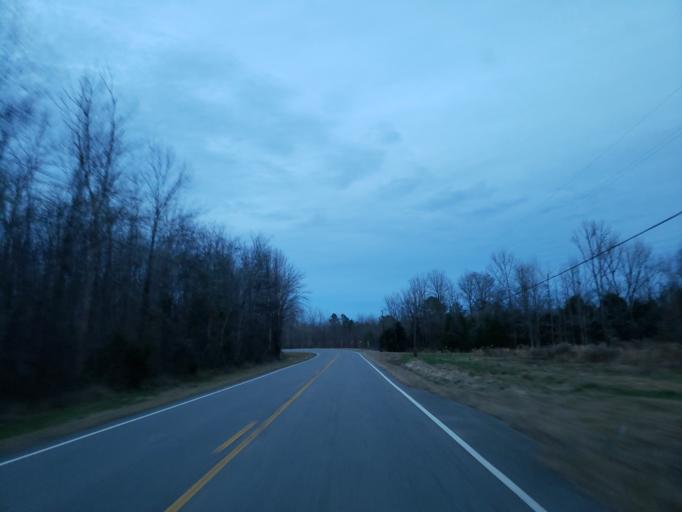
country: US
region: Alabama
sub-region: Greene County
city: Eutaw
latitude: 32.8543
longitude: -88.1042
